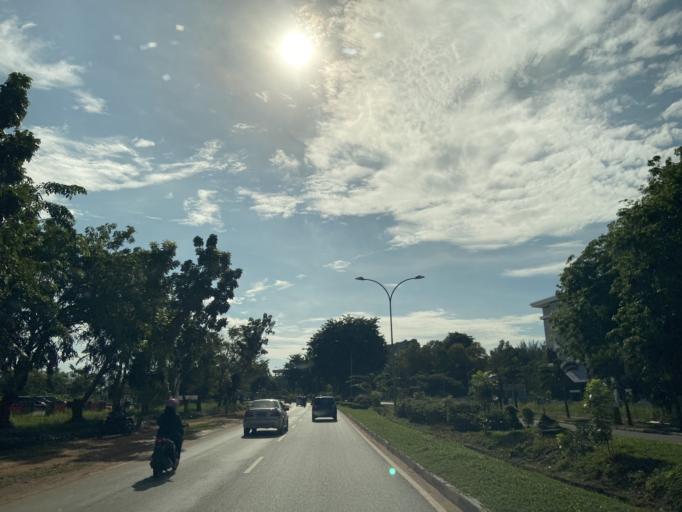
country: SG
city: Singapore
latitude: 1.1206
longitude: 104.0494
